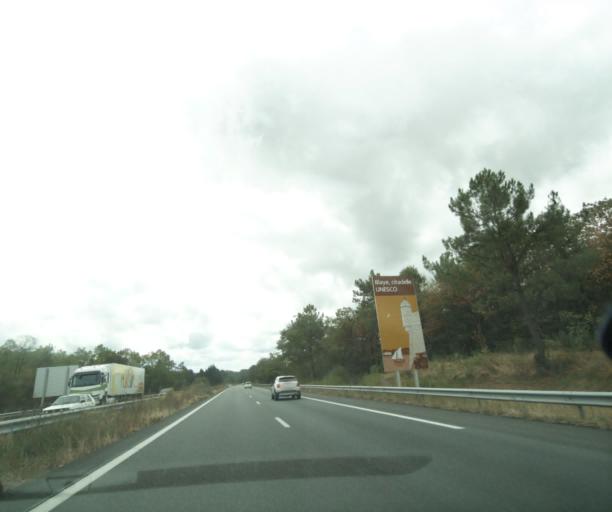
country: FR
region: Poitou-Charentes
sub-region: Departement de la Charente-Maritime
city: Mirambeau
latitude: 45.3468
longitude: -0.5775
